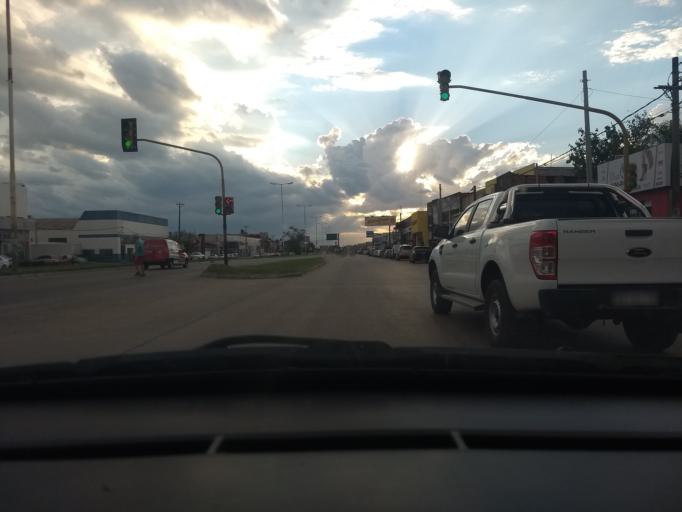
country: AR
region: Corrientes
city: Corrientes
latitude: -27.4808
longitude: -58.8005
